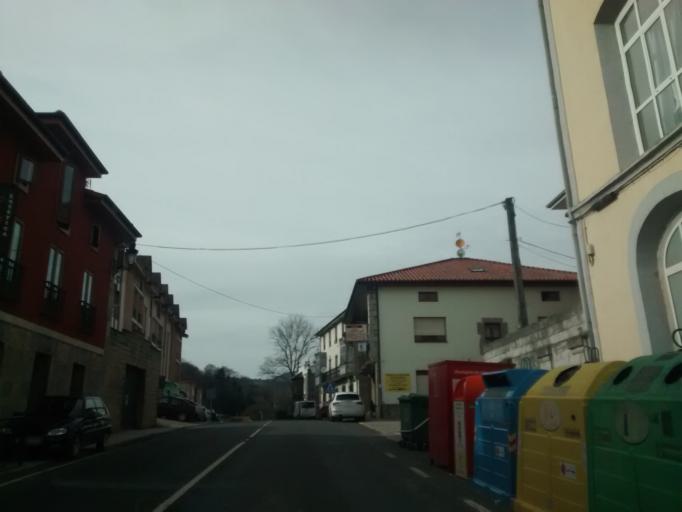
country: ES
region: Cantabria
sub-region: Provincia de Cantabria
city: Santiurde de Toranzo
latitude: 43.1978
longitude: -3.9237
